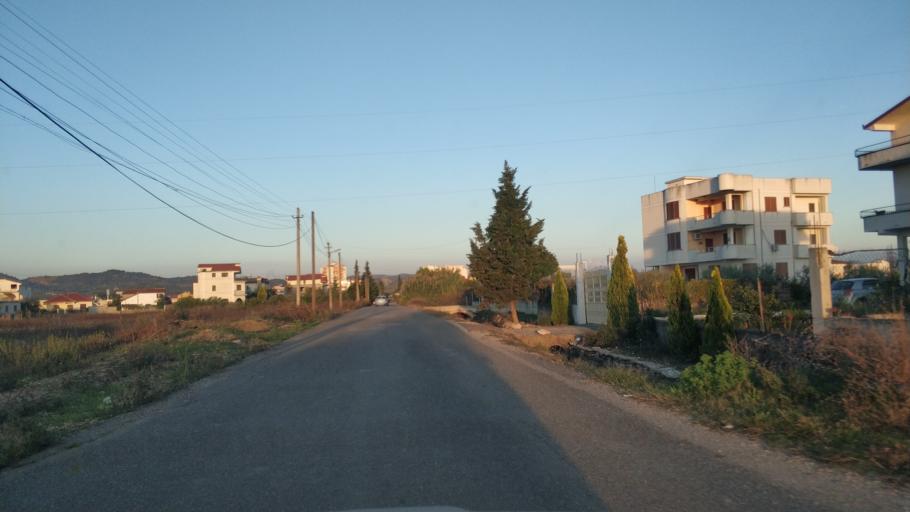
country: AL
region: Tirane
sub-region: Rrethi i Tiranes
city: Shengjergj
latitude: 41.1932
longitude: 19.5418
